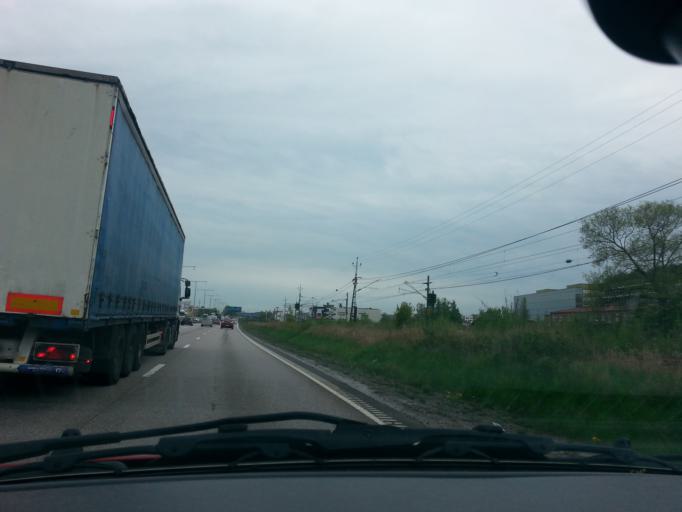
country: SE
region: Vaestra Goetaland
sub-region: Molndal
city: Moelndal
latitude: 57.6722
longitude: 12.0122
